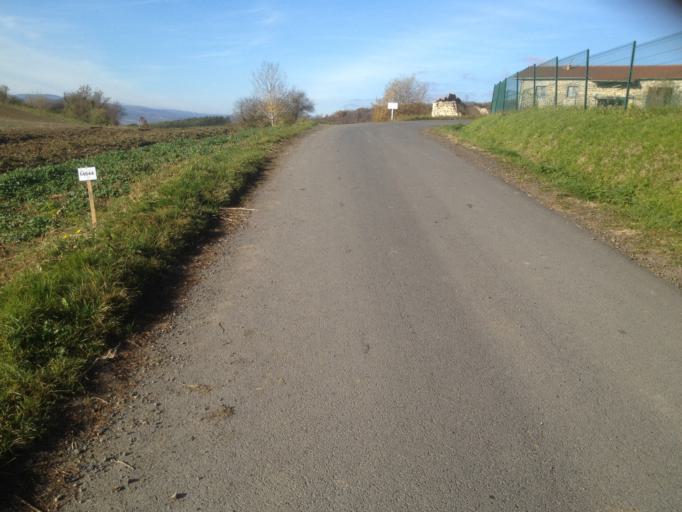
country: FR
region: Auvergne
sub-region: Departement du Puy-de-Dome
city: Issoire
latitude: 45.5711
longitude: 3.2906
